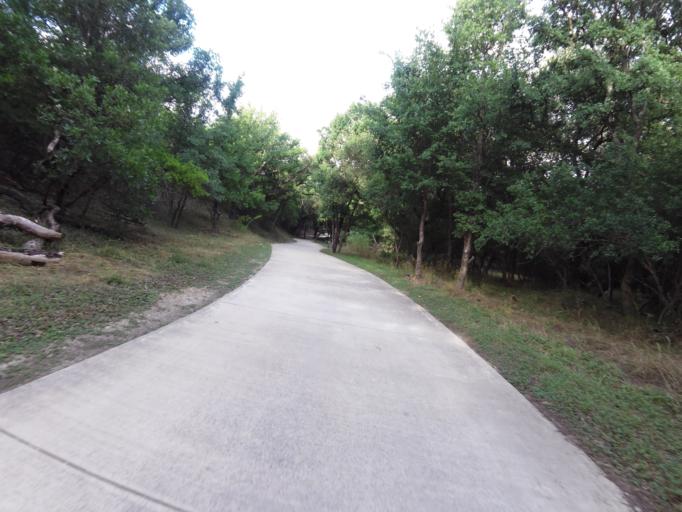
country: US
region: Texas
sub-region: Bexar County
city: Leon Valley
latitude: 29.5094
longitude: -98.6346
